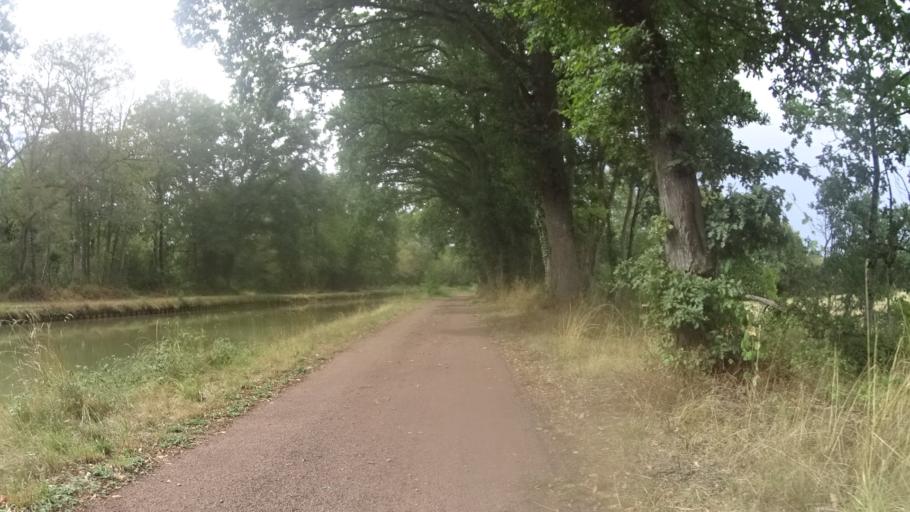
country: FR
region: Bourgogne
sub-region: Departement de la Nievre
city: Imphy
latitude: 46.9128
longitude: 3.2454
